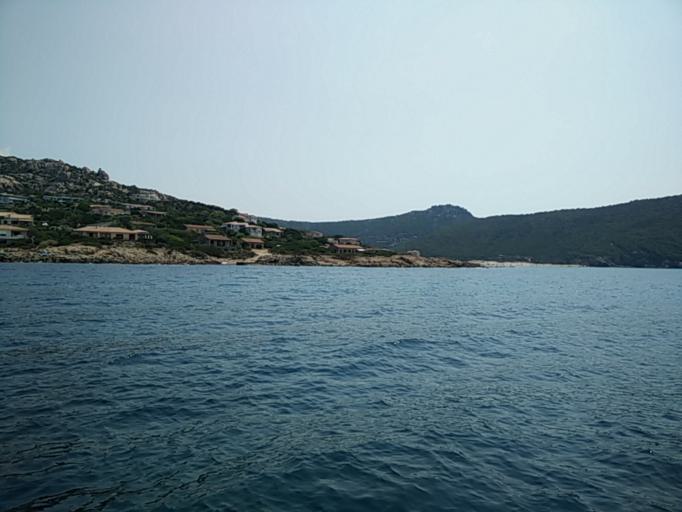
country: FR
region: Corsica
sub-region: Departement de la Corse-du-Sud
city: Propriano
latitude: 41.5397
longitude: 8.8489
